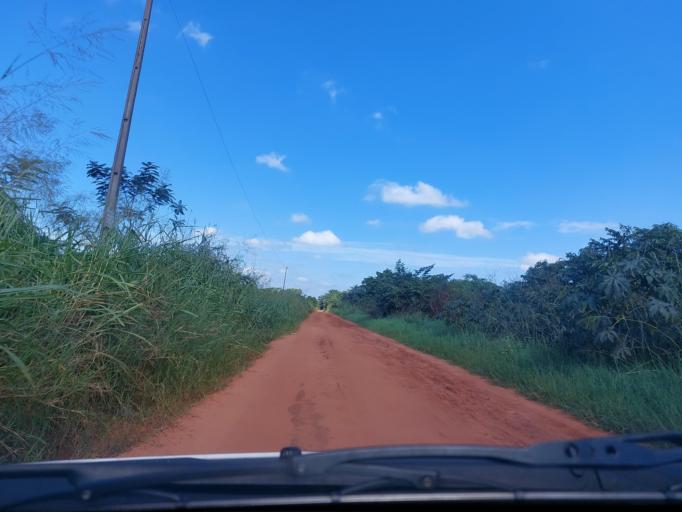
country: PY
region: San Pedro
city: Itacurubi del Rosario
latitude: -24.5319
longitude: -56.5655
